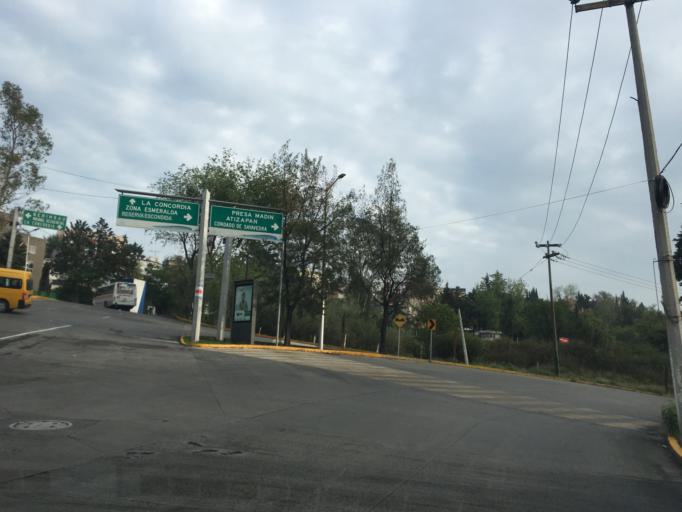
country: MX
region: Mexico
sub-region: Naucalpan de Juarez
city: Rincon Verde
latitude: 19.5175
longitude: -99.2712
